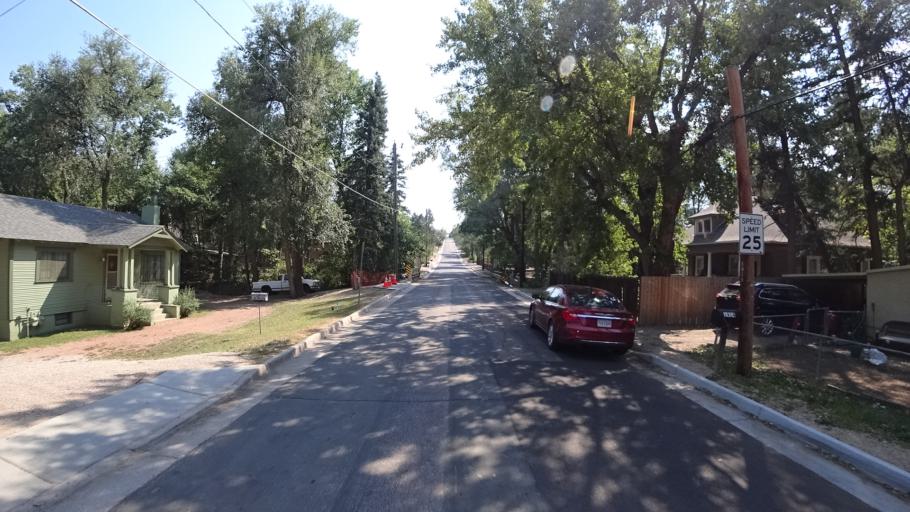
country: US
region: Colorado
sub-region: El Paso County
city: Colorado Springs
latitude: 38.8062
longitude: -104.8282
